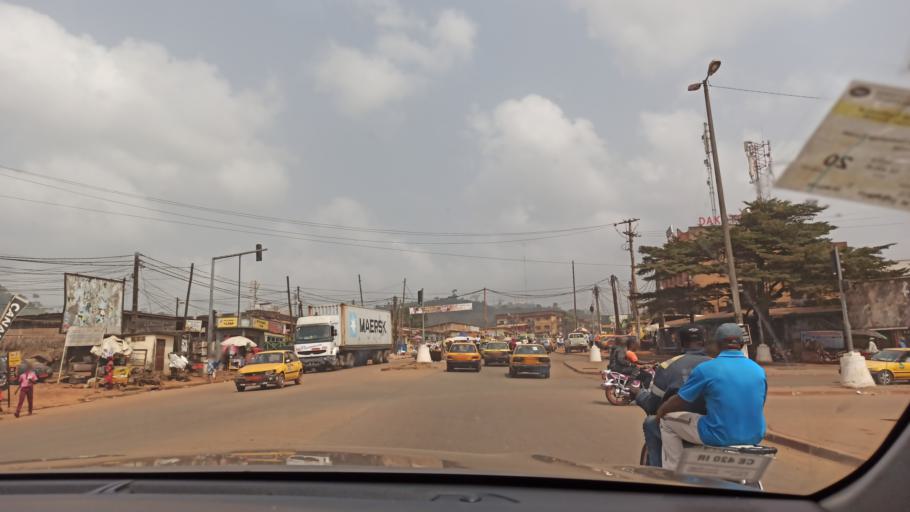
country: CM
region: Centre
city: Yaounde
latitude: 3.8825
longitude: 11.4922
